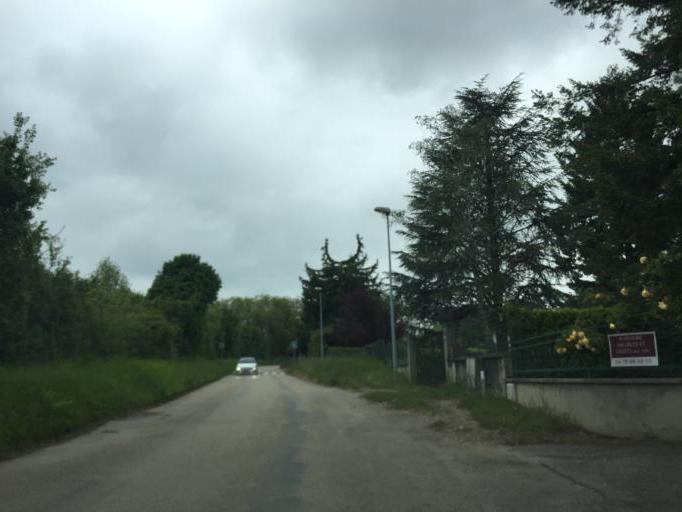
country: FR
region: Rhone-Alpes
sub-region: Departement du Rhone
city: Rillieux-la-Pape
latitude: 45.8205
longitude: 4.9214
